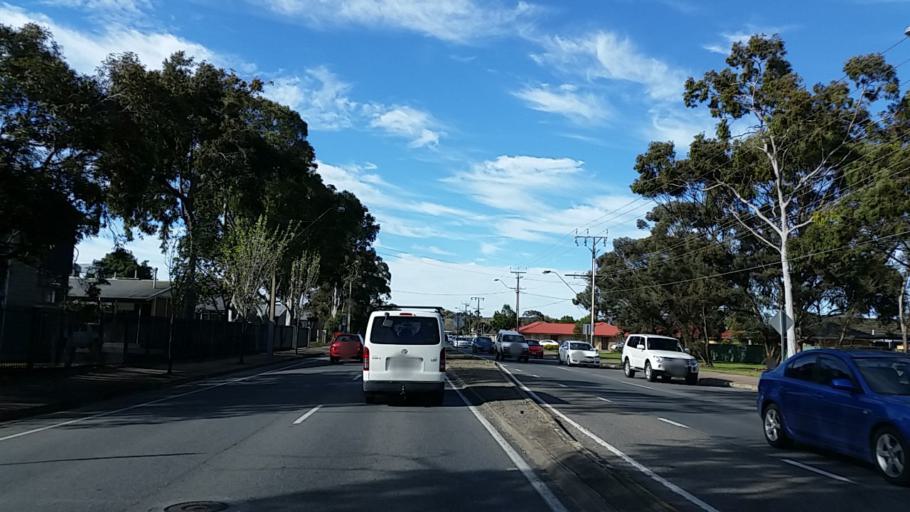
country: AU
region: South Australia
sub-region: Marion
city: Clovelly Park
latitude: -34.9976
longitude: 138.5573
